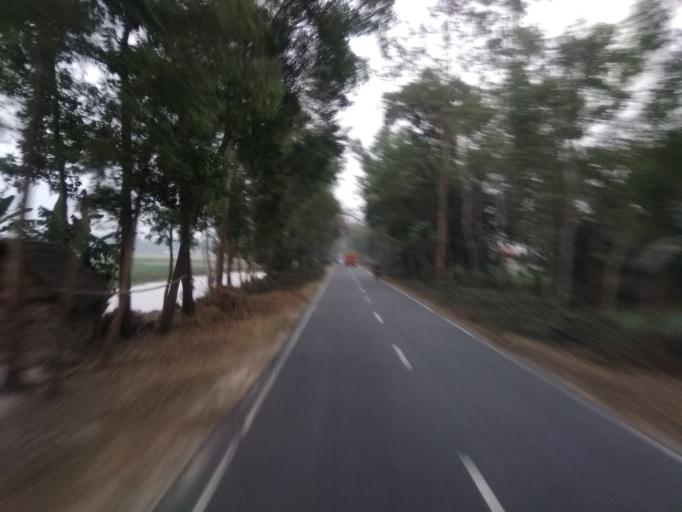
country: BD
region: Rajshahi
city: Bogra
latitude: 24.6875
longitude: 89.2934
